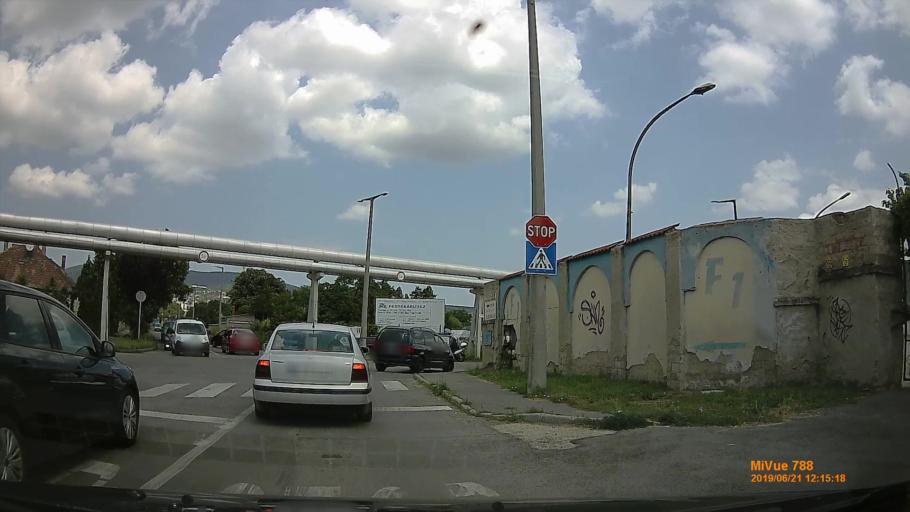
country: HU
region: Baranya
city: Pecs
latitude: 46.0623
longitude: 18.2134
